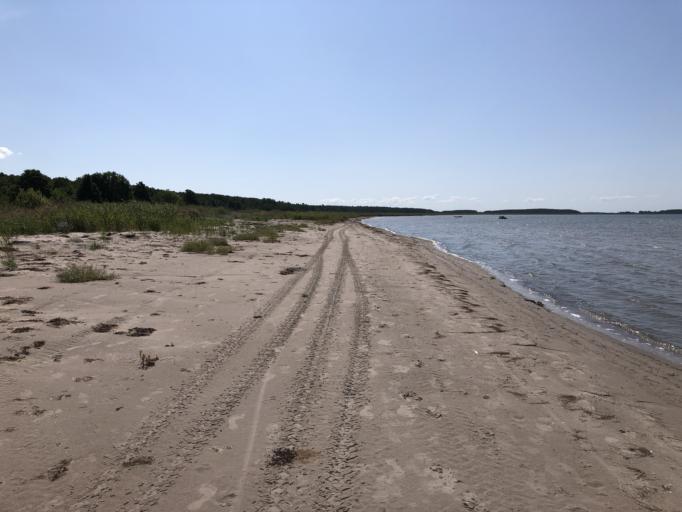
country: EE
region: Hiiumaa
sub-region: Kaerdla linn
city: Kardla
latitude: 58.7752
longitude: 22.4777
